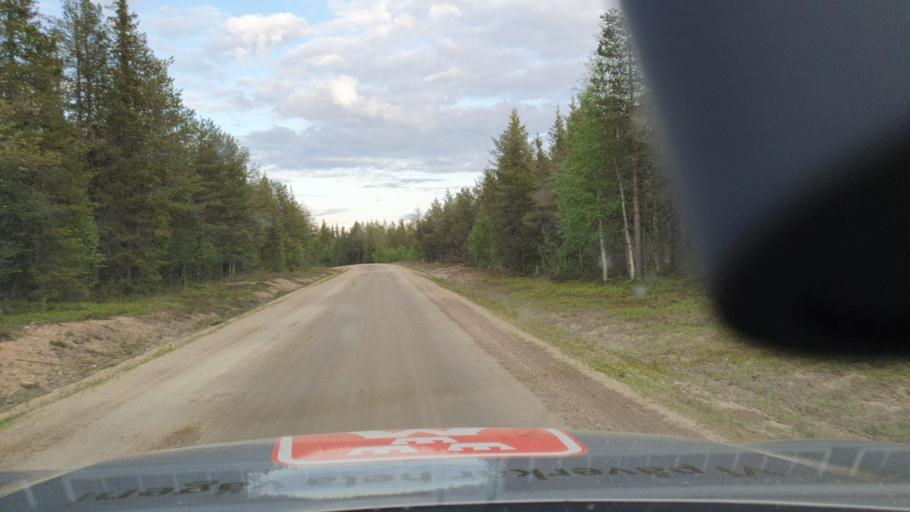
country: SE
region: Norrbotten
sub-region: Gallivare Kommun
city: Gaellivare
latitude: 66.6916
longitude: 21.1675
